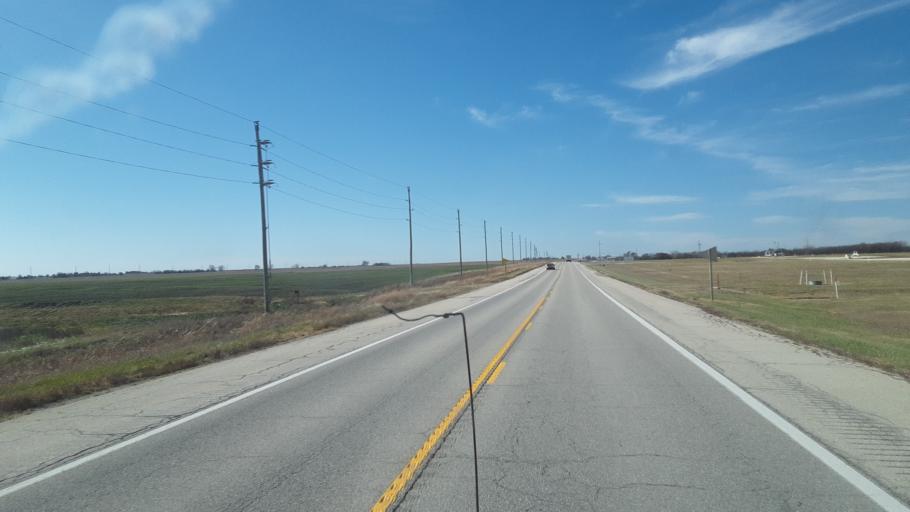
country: US
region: Kansas
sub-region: McPherson County
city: Inman
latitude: 38.3770
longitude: -97.8360
